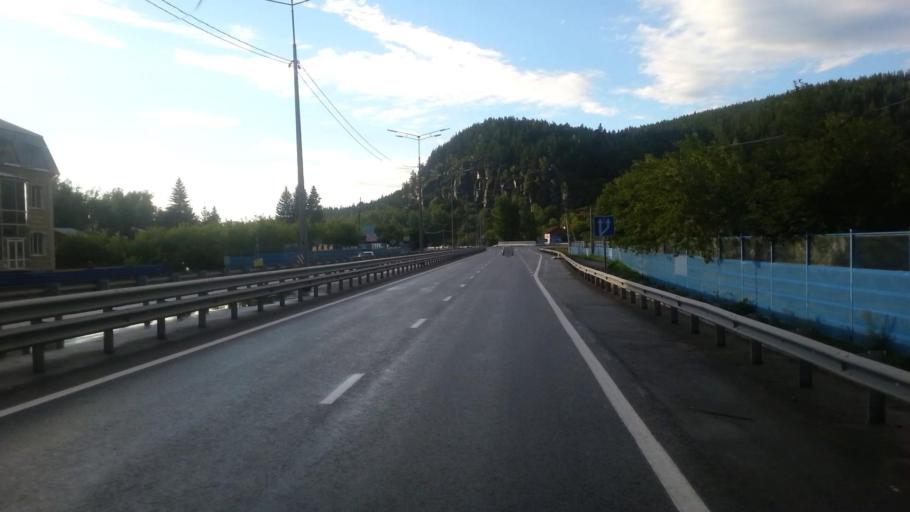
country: RU
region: Altay
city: Souzga
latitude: 51.9163
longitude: 85.8610
